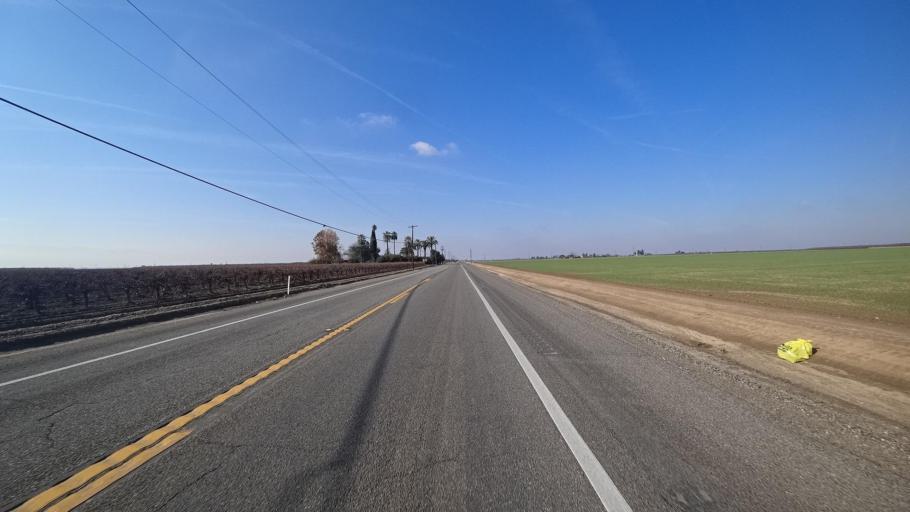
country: US
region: California
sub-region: Kern County
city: Arvin
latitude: 35.2089
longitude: -118.8700
